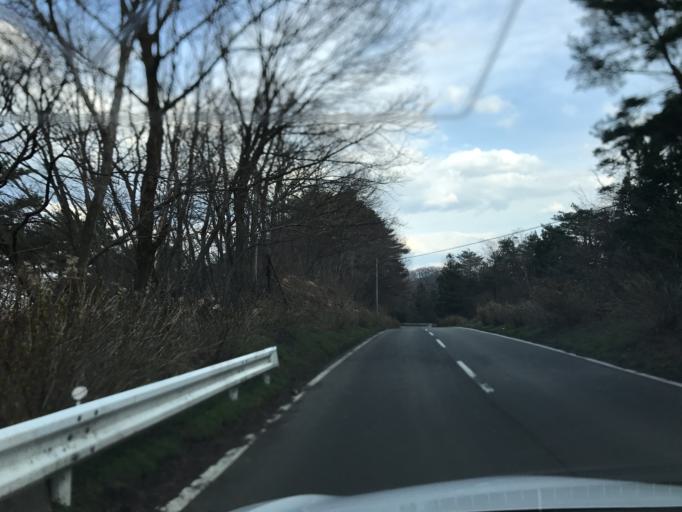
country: JP
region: Miyagi
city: Shiroishi
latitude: 38.0234
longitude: 140.5564
